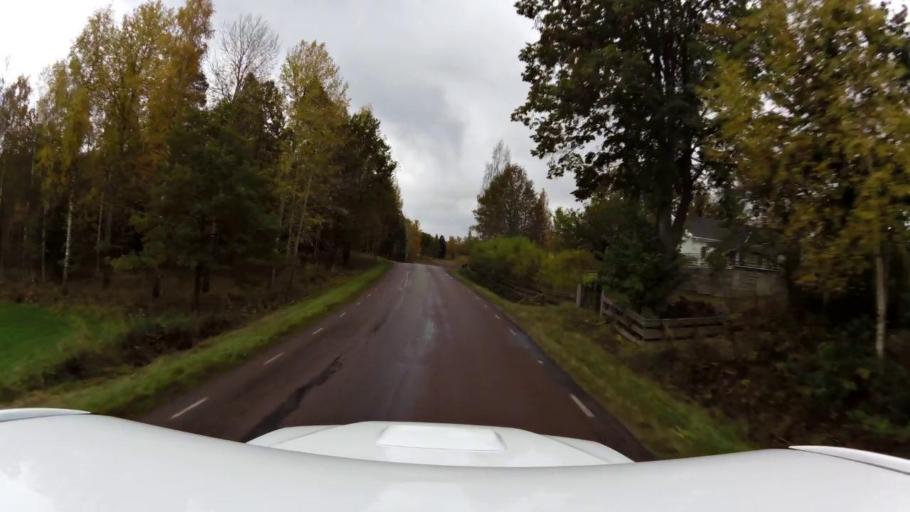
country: SE
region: OEstergoetland
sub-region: Linkopings Kommun
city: Ljungsbro
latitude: 58.5380
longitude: 15.5244
